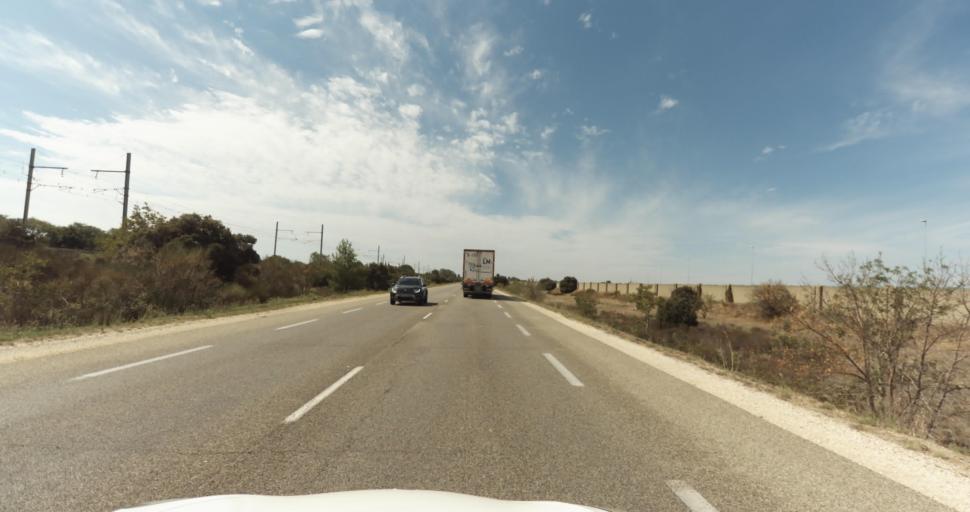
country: FR
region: Provence-Alpes-Cote d'Azur
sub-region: Departement des Bouches-du-Rhone
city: Miramas
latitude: 43.5657
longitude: 4.9755
